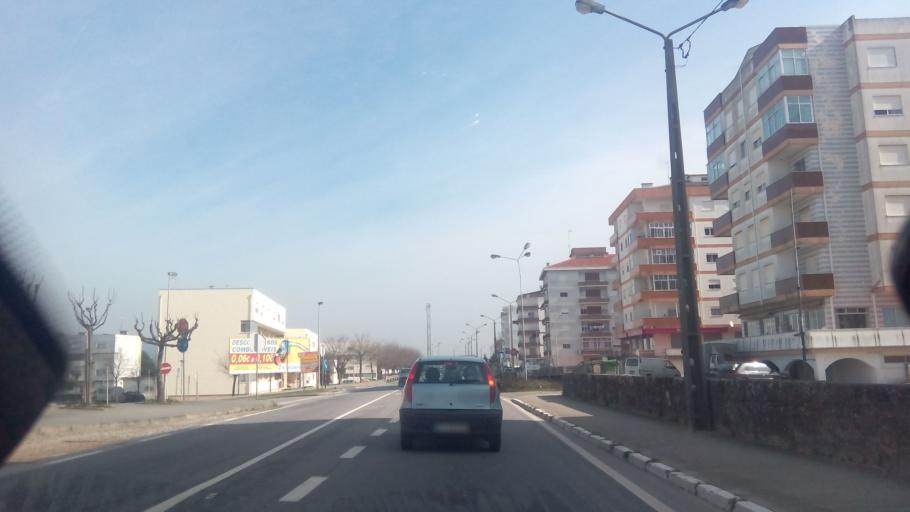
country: PT
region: Viana do Castelo
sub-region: Viana do Castelo
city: Meadela
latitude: 41.6824
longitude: -8.7978
